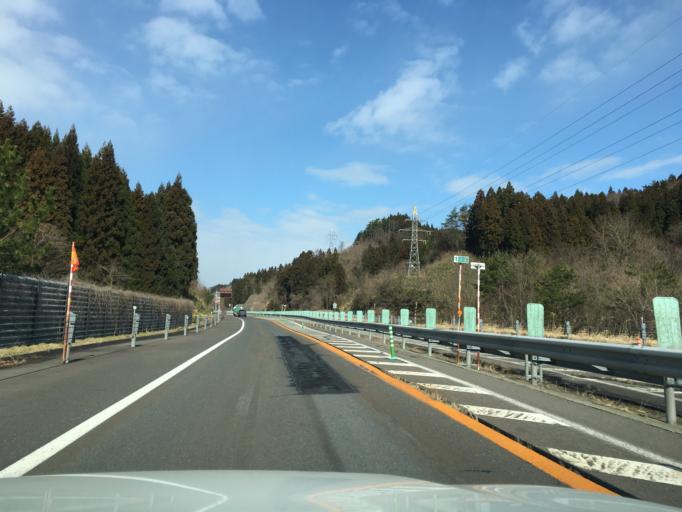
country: JP
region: Akita
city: Akita
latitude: 39.7765
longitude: 140.1185
